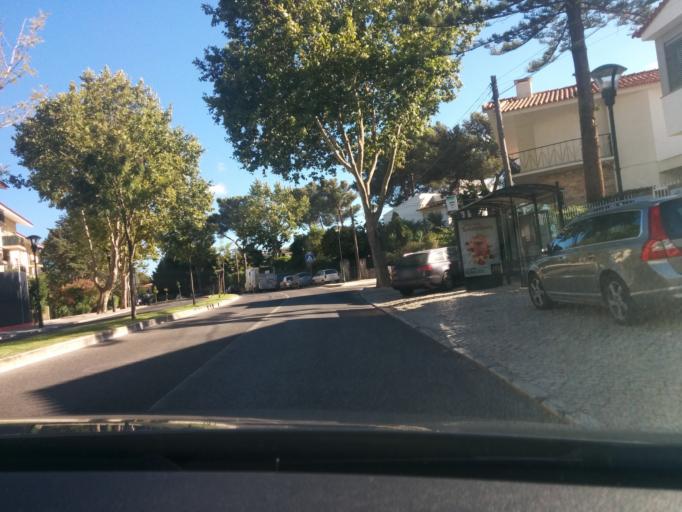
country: PT
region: Lisbon
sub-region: Cascais
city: Cascais
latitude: 38.7035
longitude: -9.4346
